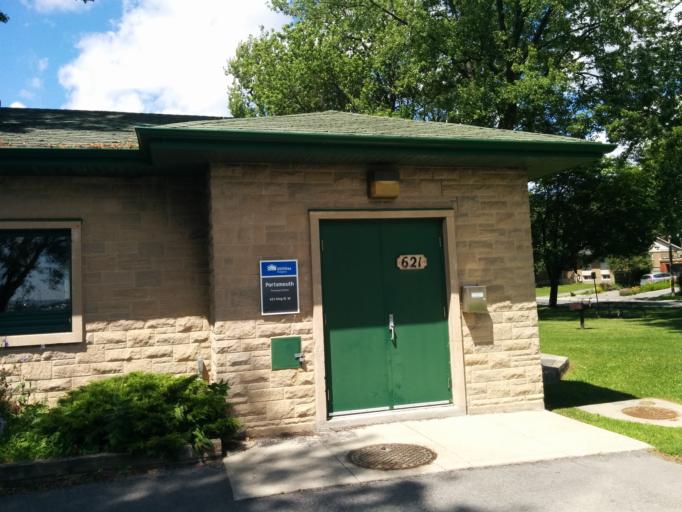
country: CA
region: Ontario
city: Kingston
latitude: 44.2212
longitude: -76.5164
